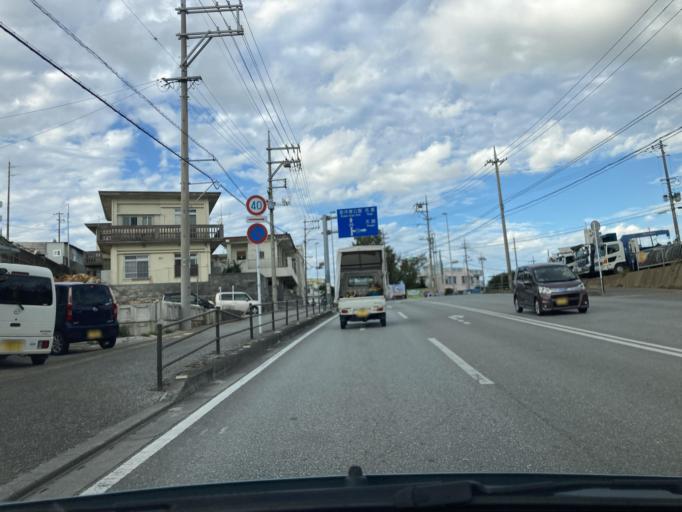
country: JP
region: Okinawa
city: Ishikawa
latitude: 26.4056
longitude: 127.8297
